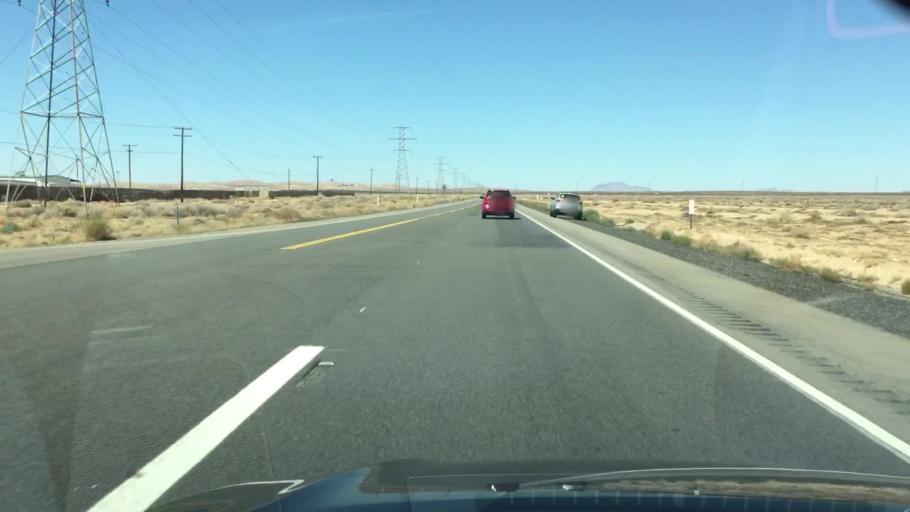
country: US
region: California
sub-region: Kern County
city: Boron
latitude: 35.0129
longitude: -117.5473
